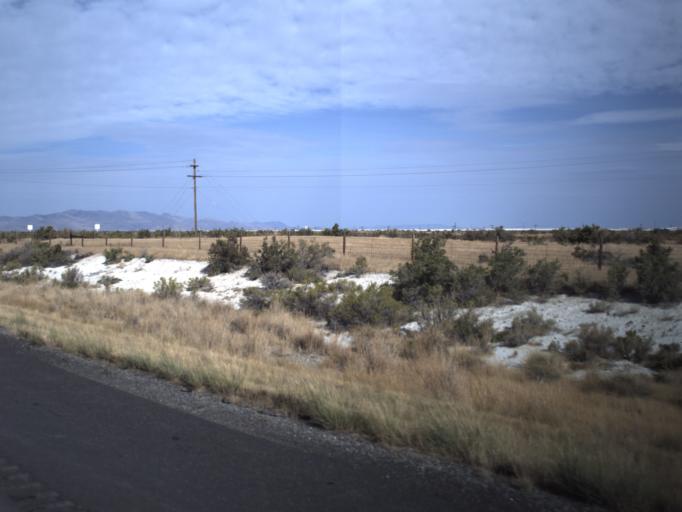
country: US
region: Utah
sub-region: Tooele County
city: Grantsville
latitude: 40.7055
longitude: -112.5135
